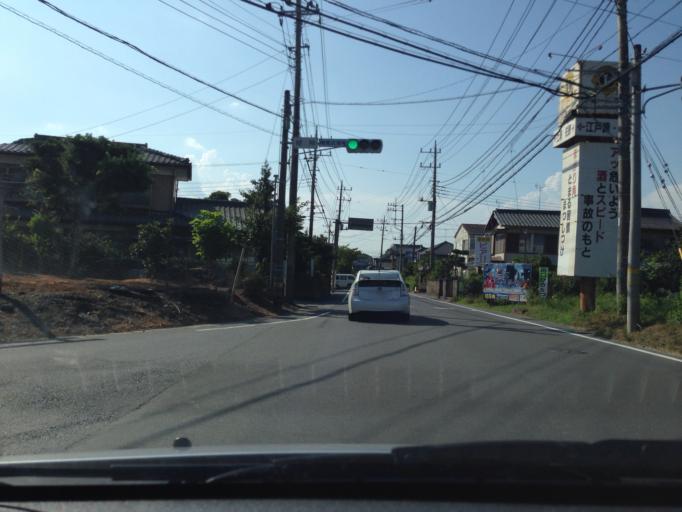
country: JP
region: Ibaraki
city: Inashiki
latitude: 35.9960
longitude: 140.3287
